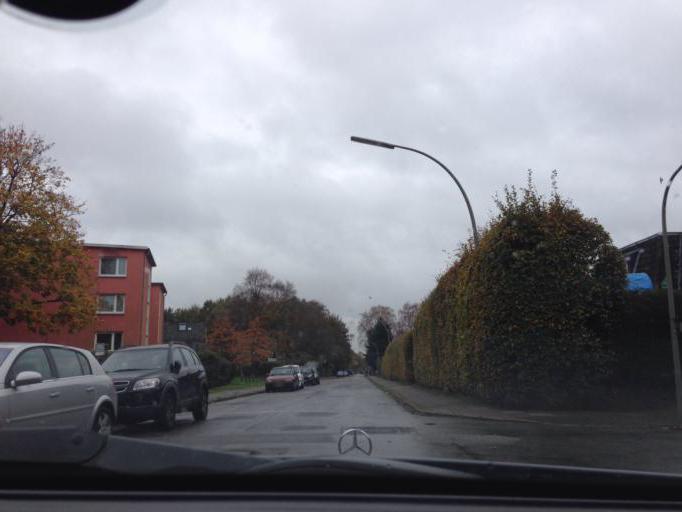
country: DE
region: Schleswig-Holstein
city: Barsbuettel
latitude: 53.5916
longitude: 10.1590
